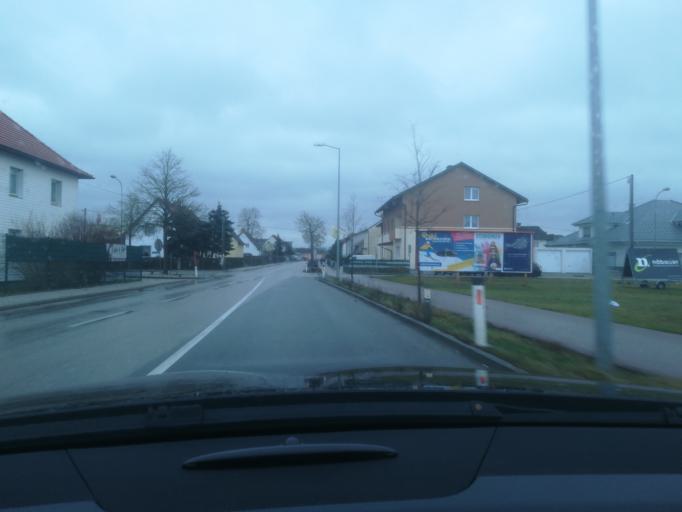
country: AT
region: Upper Austria
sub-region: Wels-Land
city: Marchtrenk
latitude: 48.1945
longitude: 14.1163
